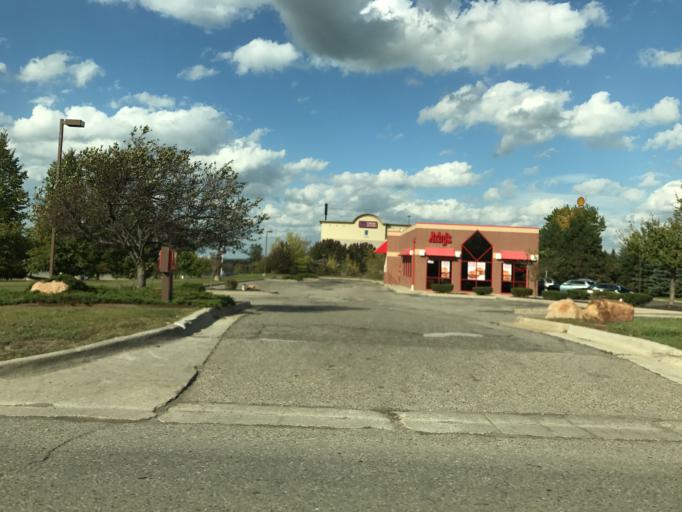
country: US
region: Michigan
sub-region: Oakland County
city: Wixom
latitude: 42.4950
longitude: -83.5388
